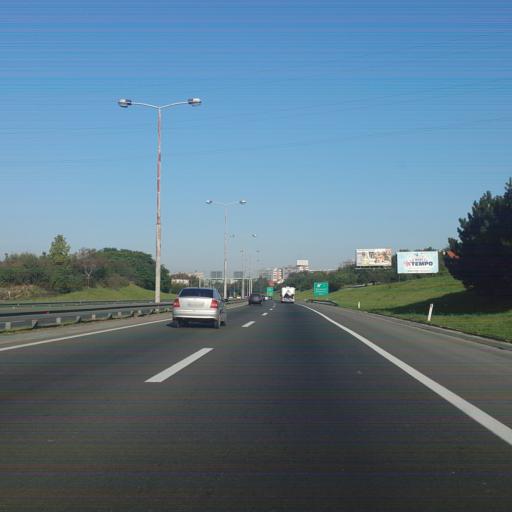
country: RS
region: Central Serbia
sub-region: Belgrade
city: Zvezdara
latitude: 44.7742
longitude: 20.5174
